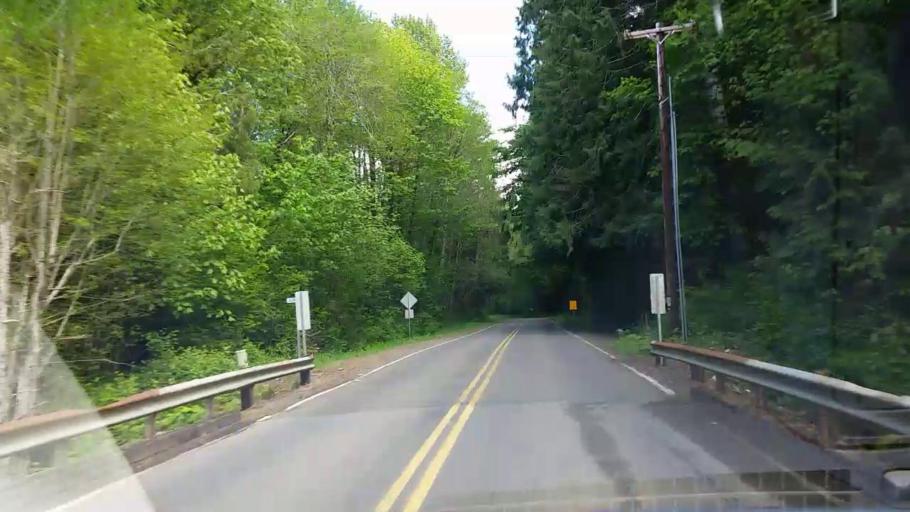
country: US
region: Washington
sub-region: Mason County
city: Shelton
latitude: 47.3157
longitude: -123.2552
